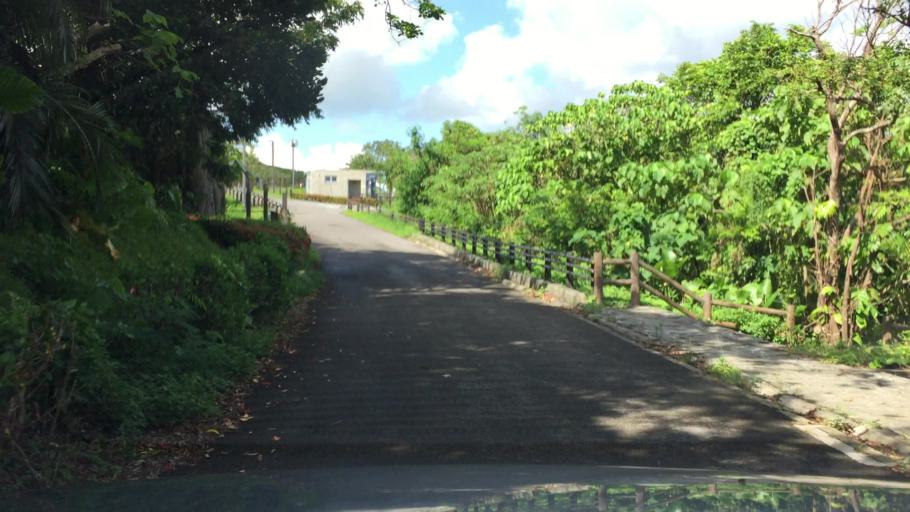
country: JP
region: Okinawa
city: Ishigaki
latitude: 24.3859
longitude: 124.1610
